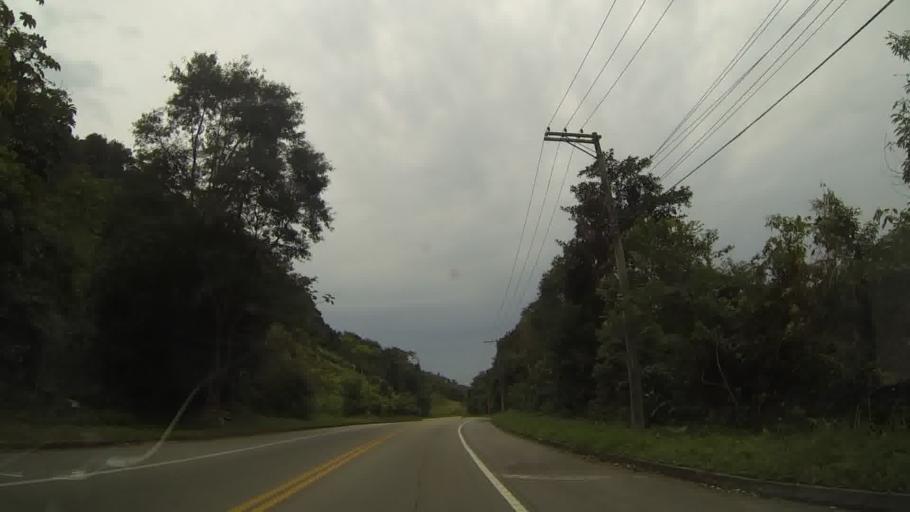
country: BR
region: Sao Paulo
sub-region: Sao Sebastiao
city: Sao Sebastiao
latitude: -23.8153
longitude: -45.4642
